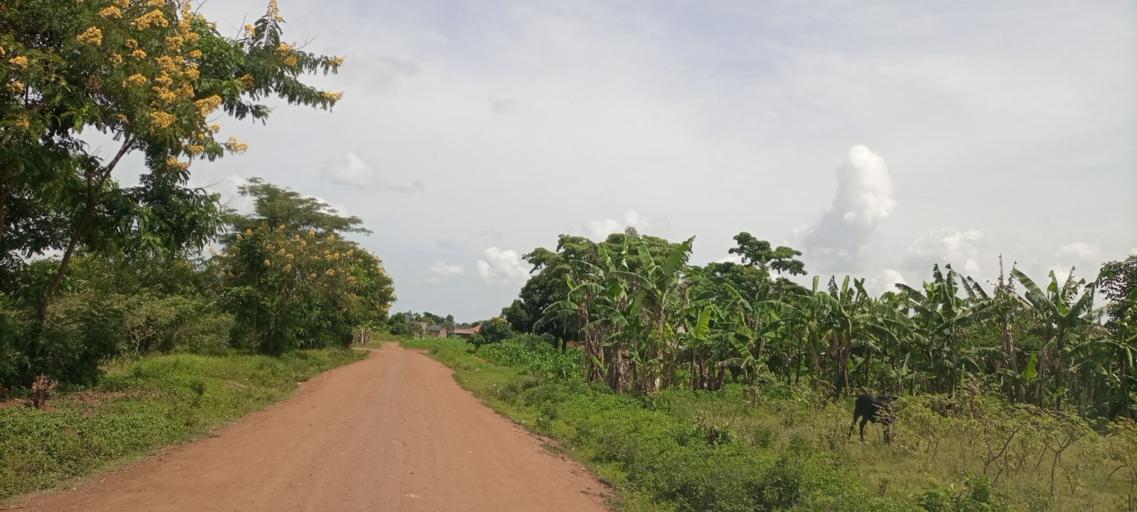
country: UG
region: Eastern Region
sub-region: Budaka District
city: Budaka
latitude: 1.1709
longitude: 33.9362
